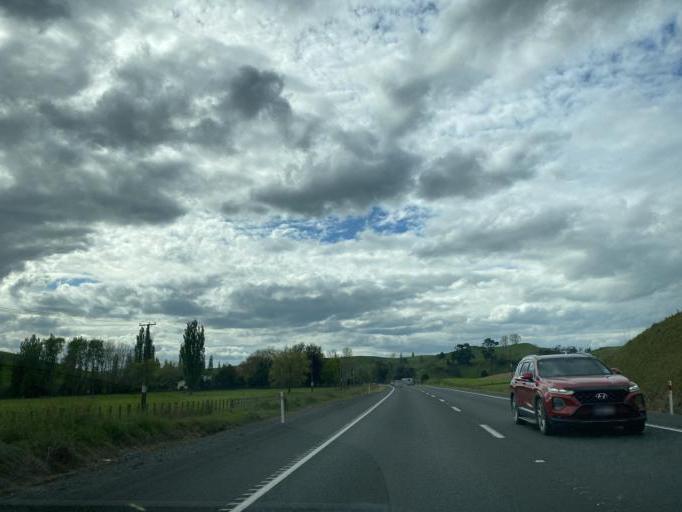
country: NZ
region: Waikato
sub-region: Matamata-Piako District
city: Matamata
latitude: -37.9621
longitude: 175.6875
